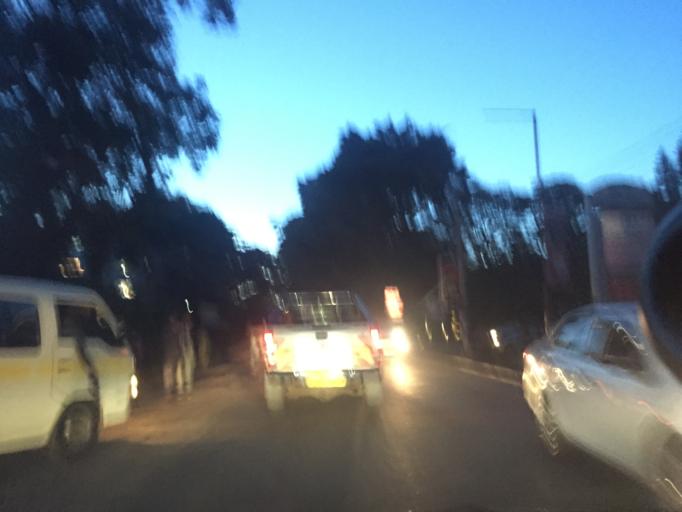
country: KE
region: Nairobi Area
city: Nairobi
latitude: -1.2901
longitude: 36.7733
